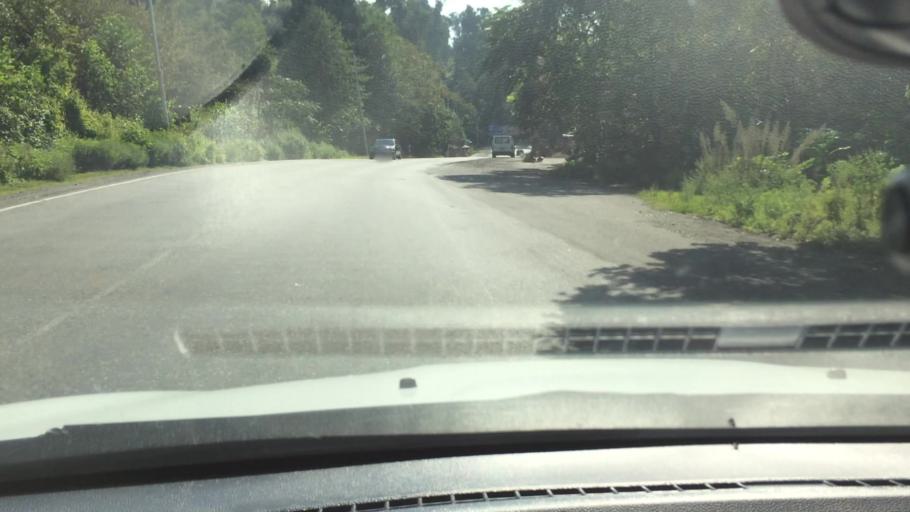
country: GE
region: Ajaria
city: Kobuleti
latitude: 41.7666
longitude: 41.7536
